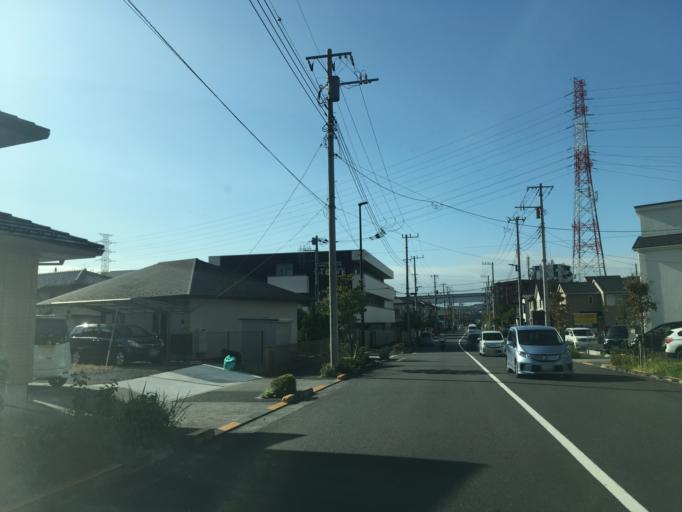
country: JP
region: Tokyo
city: Hino
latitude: 35.6798
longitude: 139.4107
